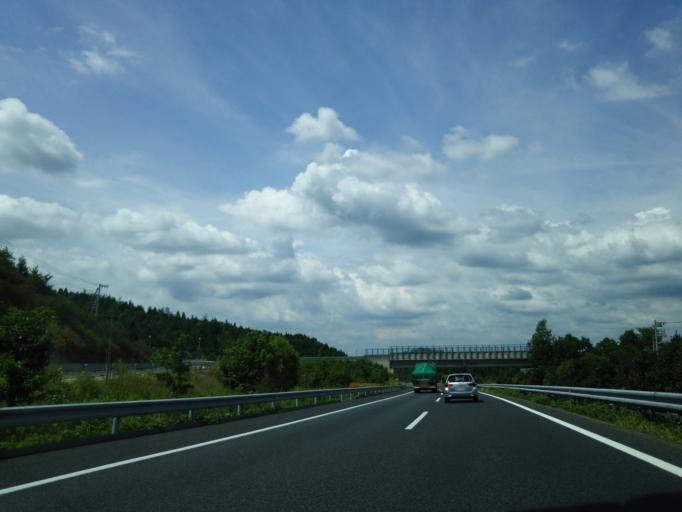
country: JP
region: Gifu
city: Toki
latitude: 35.3317
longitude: 137.1752
